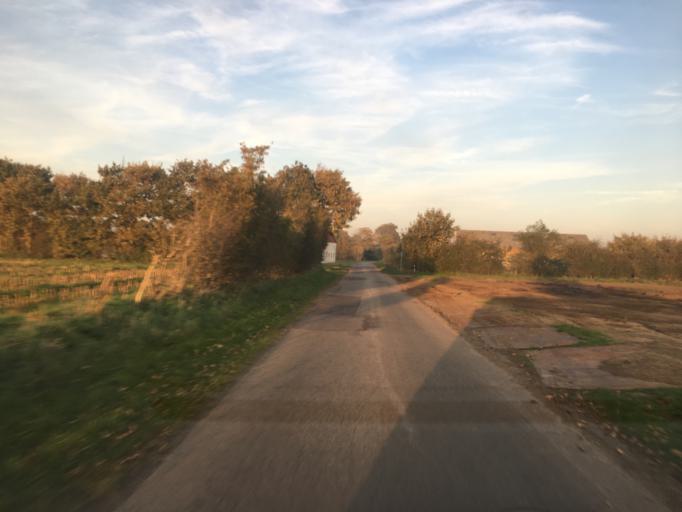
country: DK
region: South Denmark
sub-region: Tonder Kommune
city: Logumkloster
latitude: 55.0455
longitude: 9.0945
